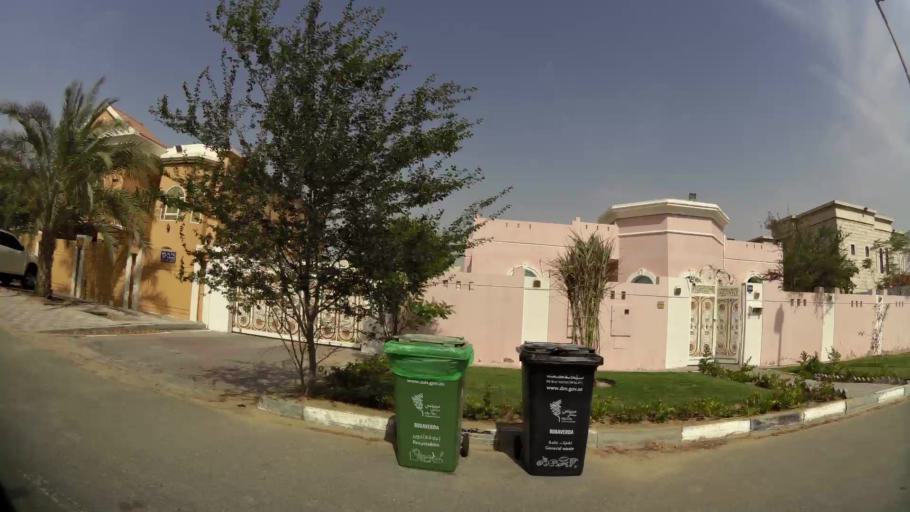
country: AE
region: Ash Shariqah
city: Sharjah
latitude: 25.2532
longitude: 55.4375
